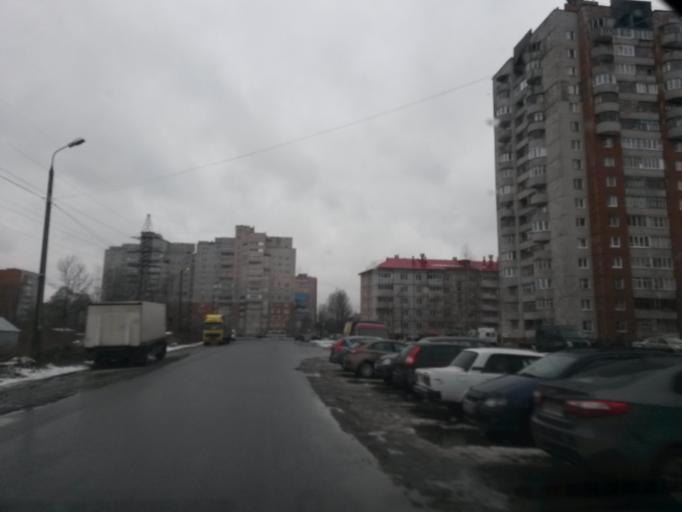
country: RU
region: Jaroslavl
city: Yaroslavl
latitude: 57.6458
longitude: 39.9591
